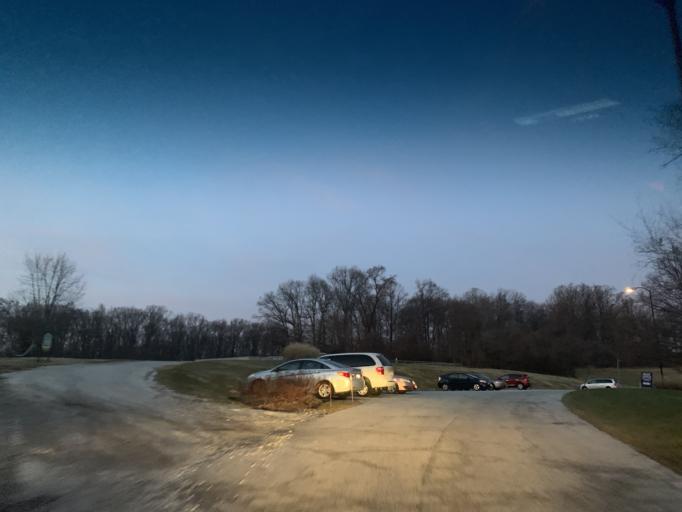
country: US
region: Maryland
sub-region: Baltimore County
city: Carney
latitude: 39.4484
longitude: -76.5179
